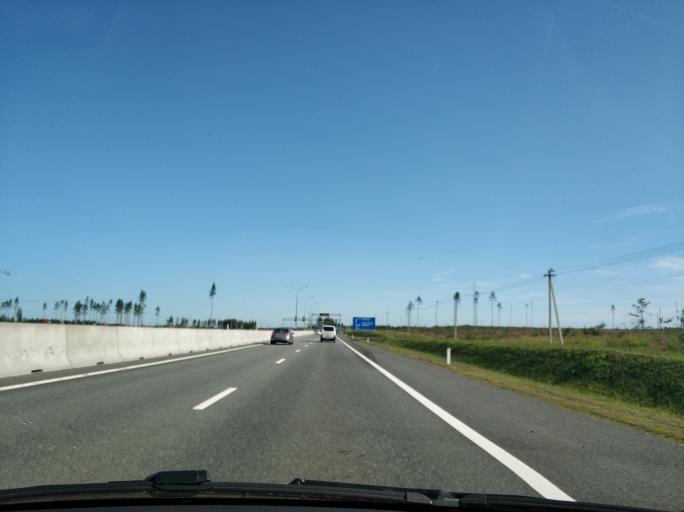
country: RU
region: Leningrad
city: Sosnovo
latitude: 60.4956
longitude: 30.1958
